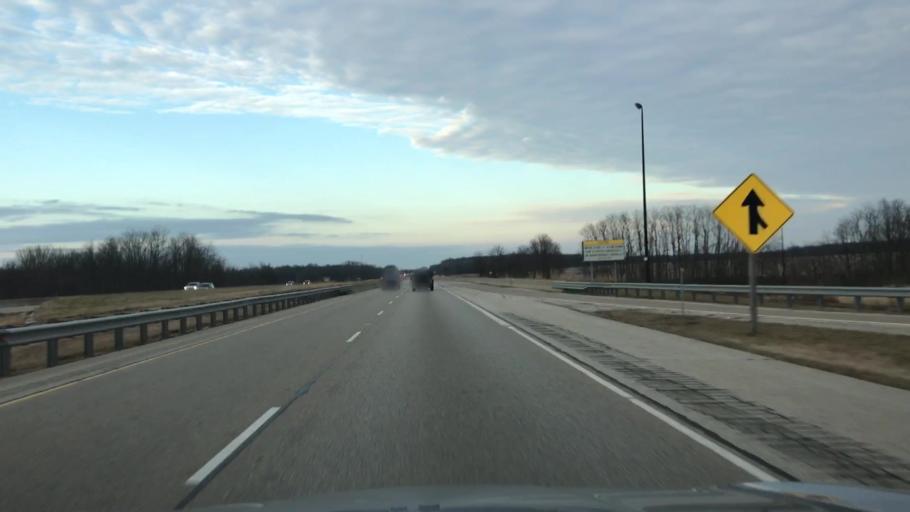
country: US
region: Illinois
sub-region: McLean County
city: Twin Grove
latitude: 40.3616
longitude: -89.1059
